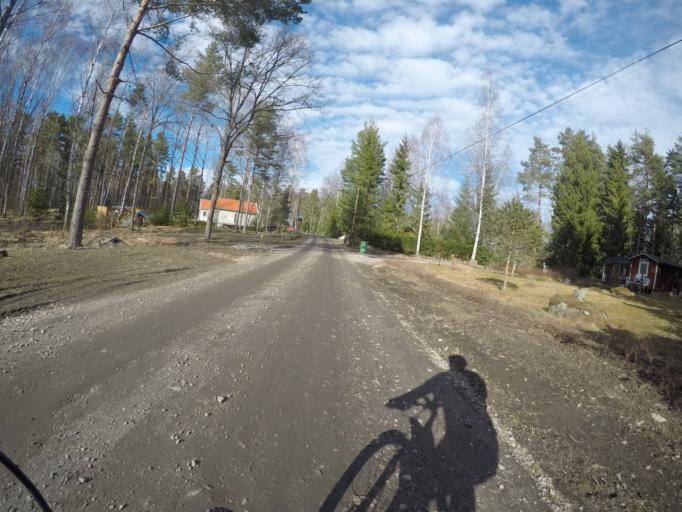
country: SE
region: Vaestmanland
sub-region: Kungsors Kommun
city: Kungsoer
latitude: 59.4327
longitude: 16.1409
